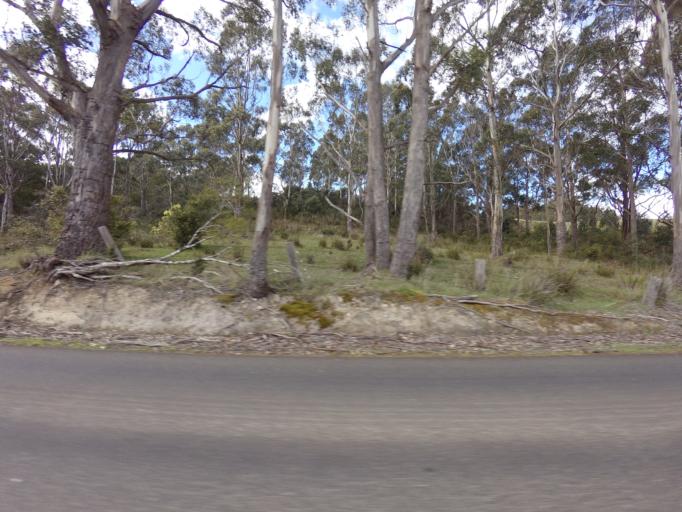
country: AU
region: Tasmania
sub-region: Huon Valley
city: Geeveston
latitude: -43.1894
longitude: 146.9356
